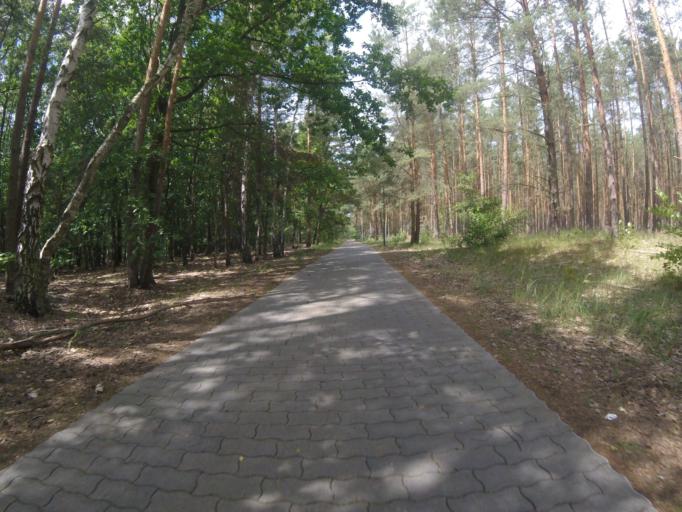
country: DE
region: Brandenburg
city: Bestensee
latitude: 52.2378
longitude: 13.6632
